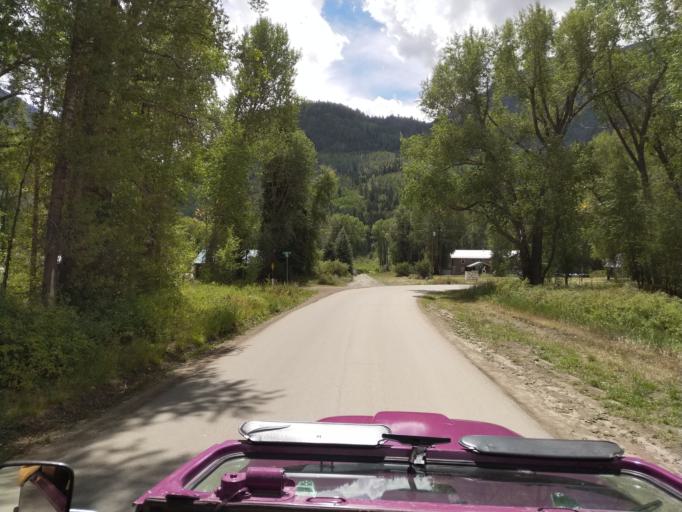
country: US
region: Colorado
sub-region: Gunnison County
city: Crested Butte
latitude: 39.0723
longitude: -107.1843
